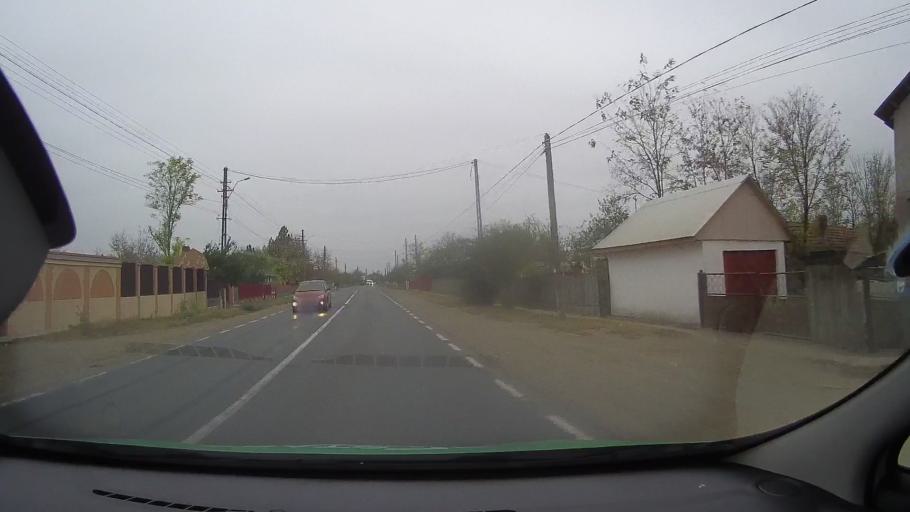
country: RO
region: Braila
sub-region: Comuna Baraganul
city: Baraganul
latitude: 44.8100
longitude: 27.5137
